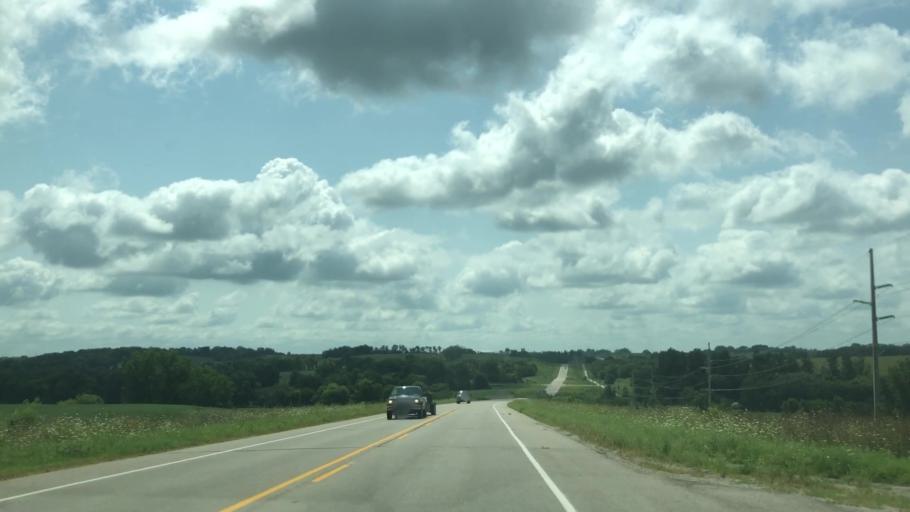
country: US
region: Iowa
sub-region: Marshall County
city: Marshalltown
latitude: 42.0245
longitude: -92.9602
